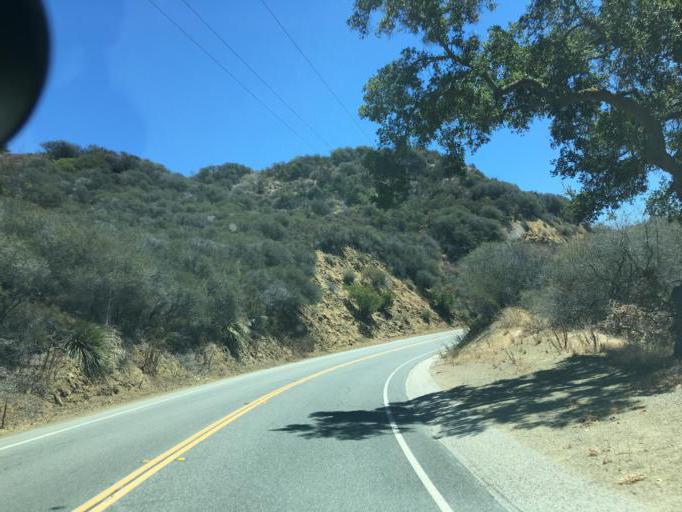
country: US
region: California
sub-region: Los Angeles County
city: Malibu
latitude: 34.0652
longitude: -118.8725
